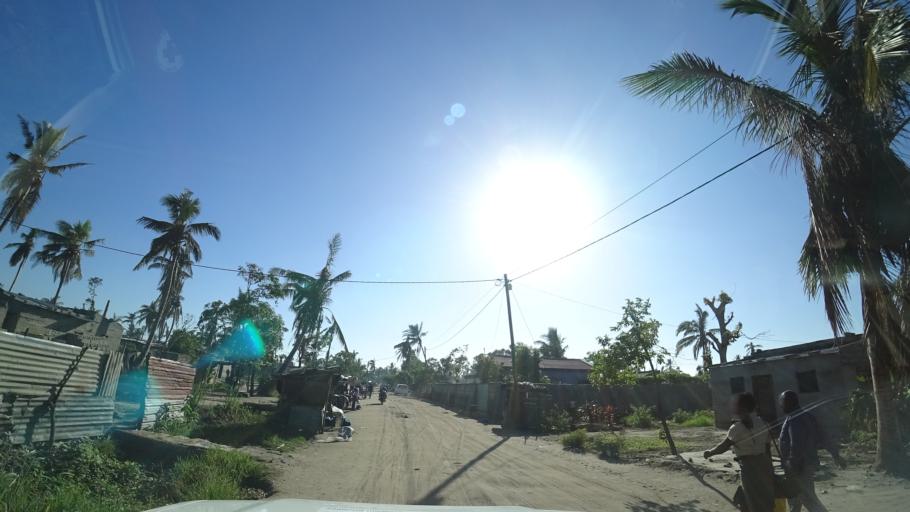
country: MZ
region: Sofala
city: Beira
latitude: -19.7730
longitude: 34.8856
